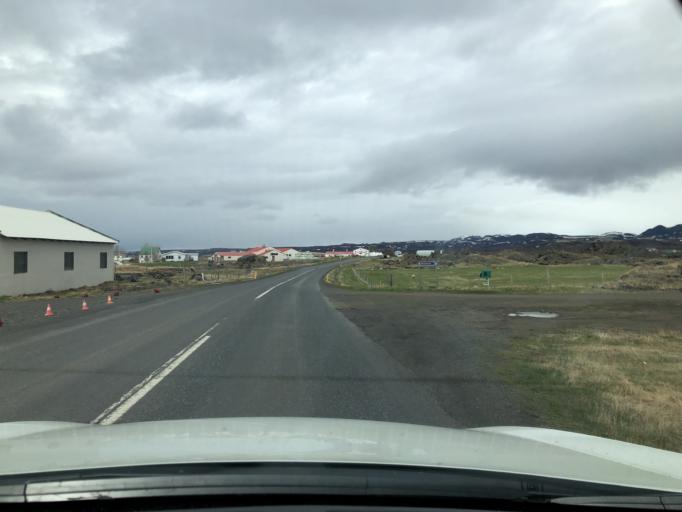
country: IS
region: Northeast
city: Laugar
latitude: 65.6191
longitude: -16.9183
